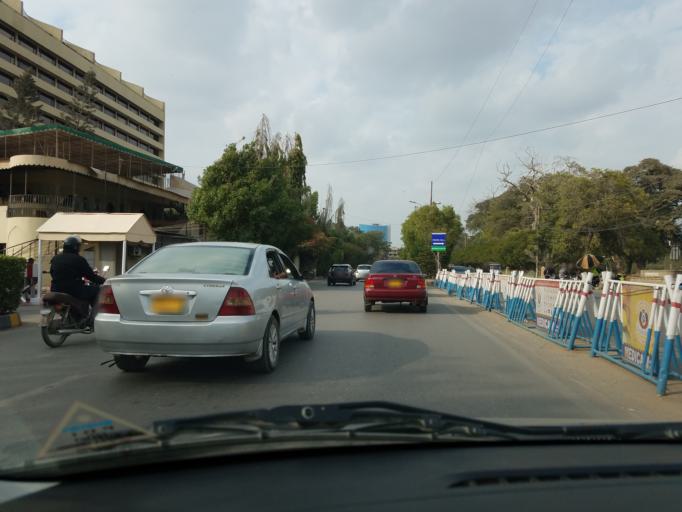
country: PK
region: Sindh
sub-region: Karachi District
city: Karachi
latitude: 24.8461
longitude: 67.0316
